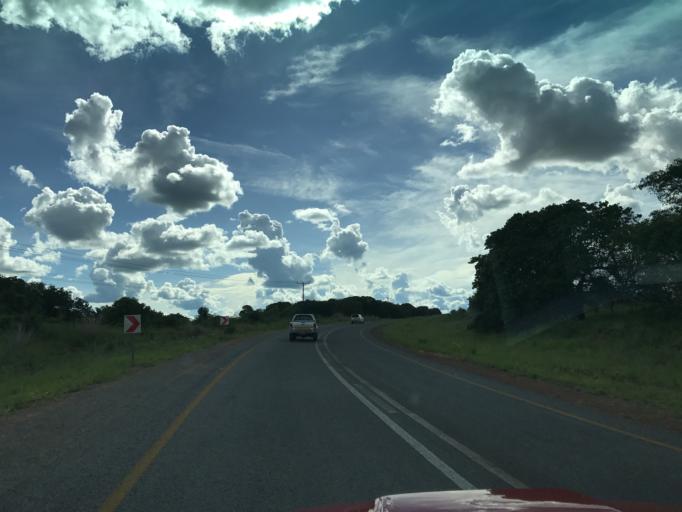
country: MZ
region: Nampula
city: Nampula
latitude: -15.0049
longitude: 38.9878
